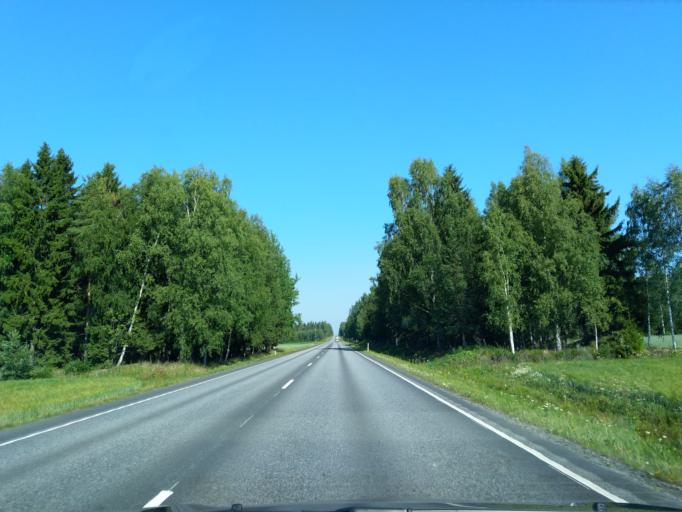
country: FI
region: Varsinais-Suomi
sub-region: Loimaa
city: Alastaro
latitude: 61.0671
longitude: 22.9282
